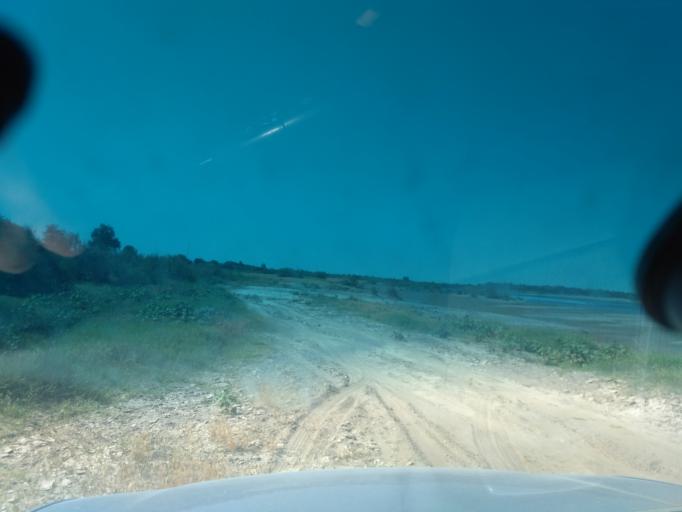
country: TJ
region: Viloyati Sughd
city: Buston
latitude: 40.5584
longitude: 69.0752
